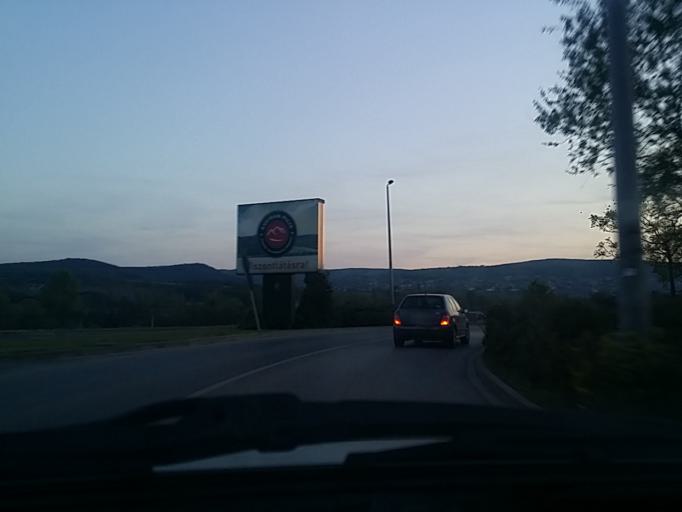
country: HU
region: Pest
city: Solymar
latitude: 47.5987
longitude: 18.9586
